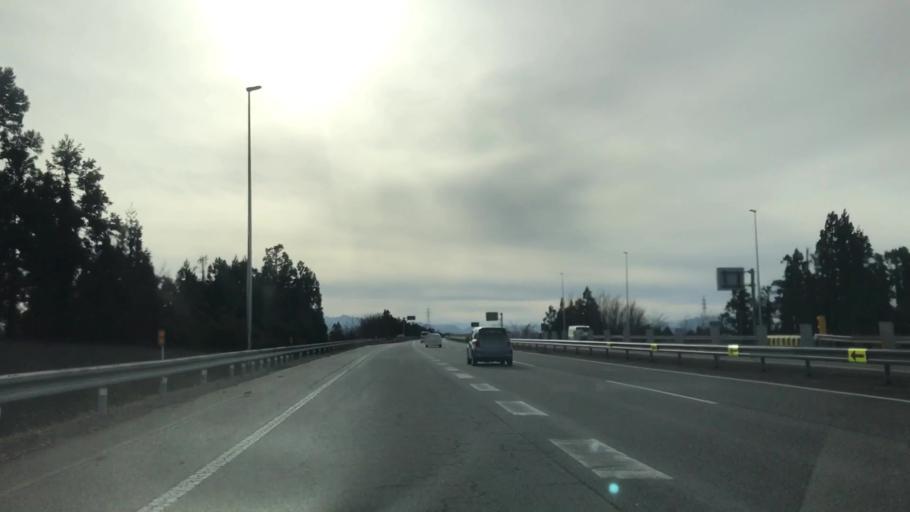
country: JP
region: Toyama
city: Kamiichi
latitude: 36.6839
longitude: 137.3240
